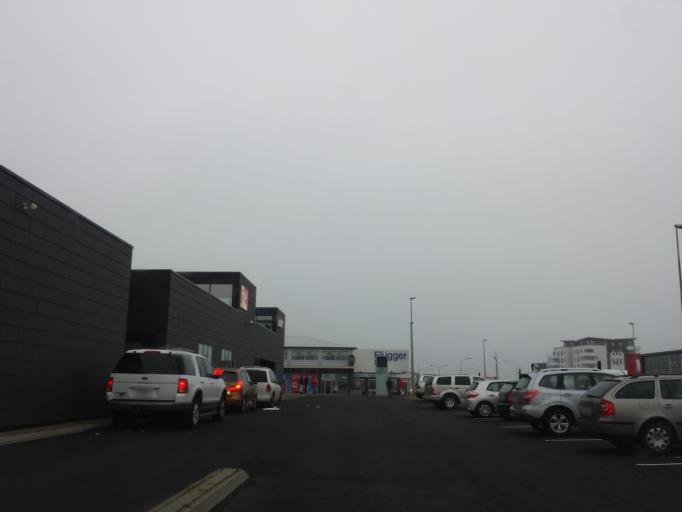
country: IS
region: Southern Peninsula
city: Reykjanesbaer
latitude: 63.9944
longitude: -22.5494
